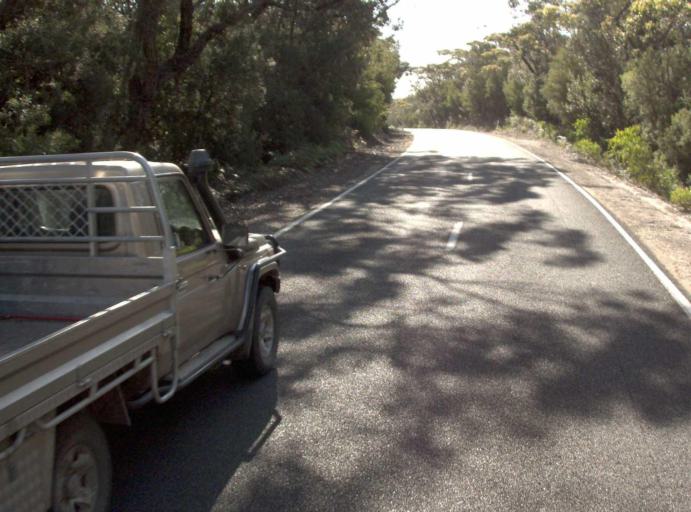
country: AU
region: Victoria
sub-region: East Gippsland
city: Lakes Entrance
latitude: -37.7982
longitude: 148.5934
